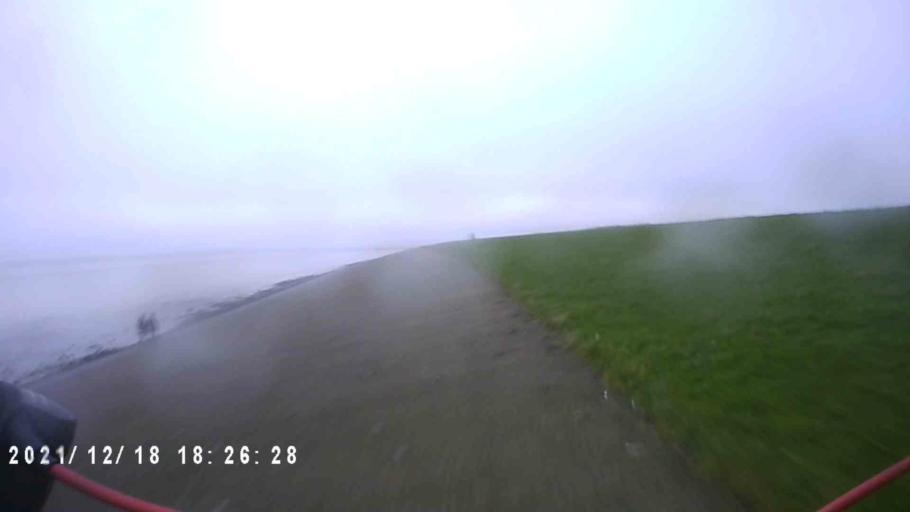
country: NL
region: Friesland
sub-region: Gemeente Dongeradeel
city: Ternaard
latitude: 53.4000
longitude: 6.0032
